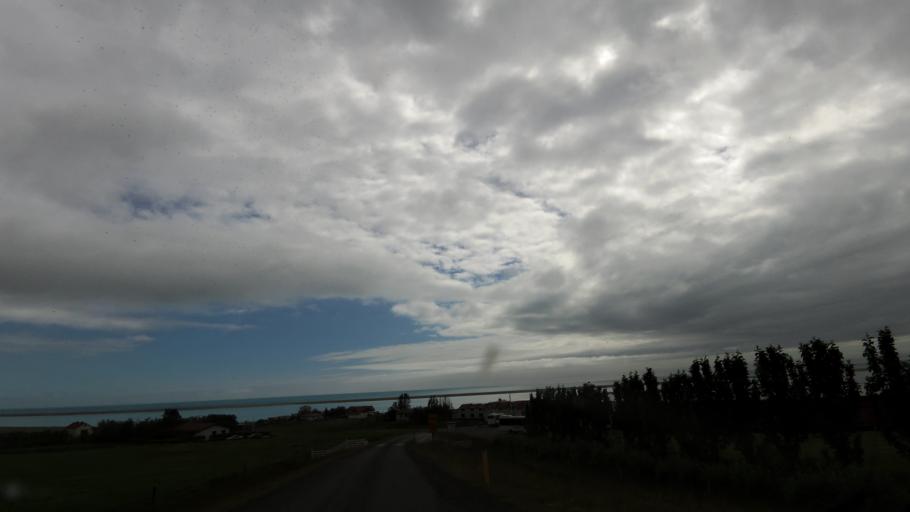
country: IS
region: East
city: Hoefn
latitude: 64.1305
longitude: -16.0187
